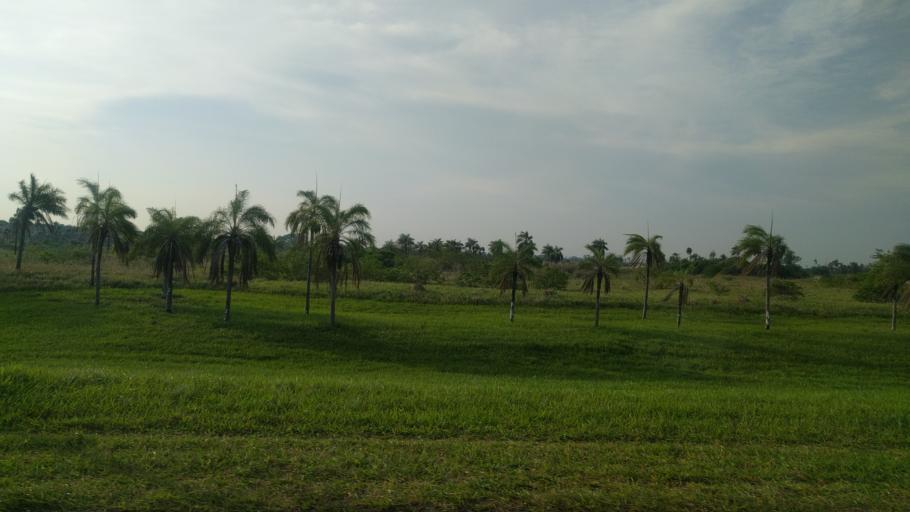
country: BO
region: Santa Cruz
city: La Belgica
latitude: -17.6544
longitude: -63.1522
